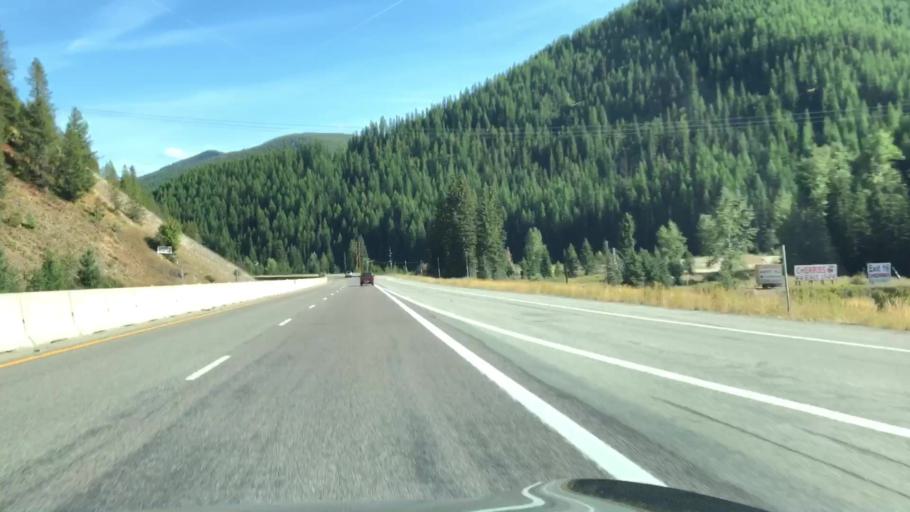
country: US
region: Montana
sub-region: Sanders County
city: Thompson Falls
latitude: 47.4209
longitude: -115.6045
